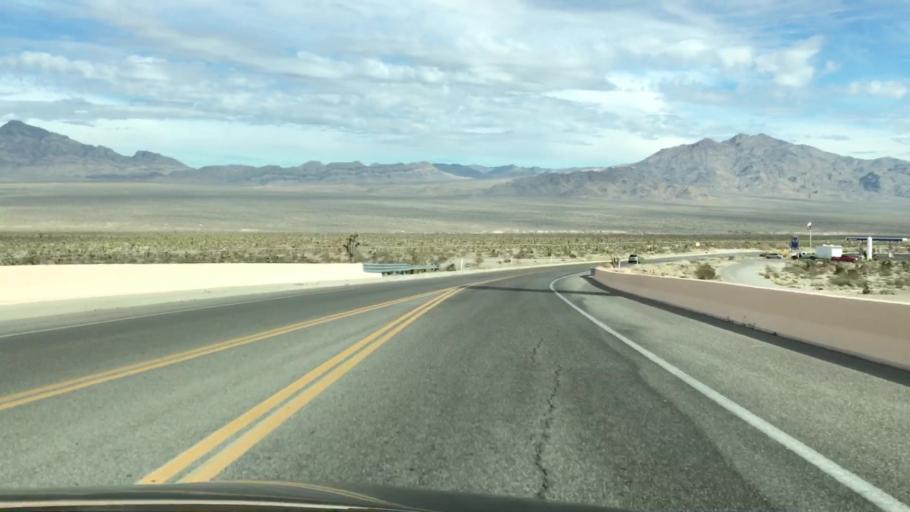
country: US
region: Nevada
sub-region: Clark County
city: Summerlin South
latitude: 36.3636
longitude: -115.3491
